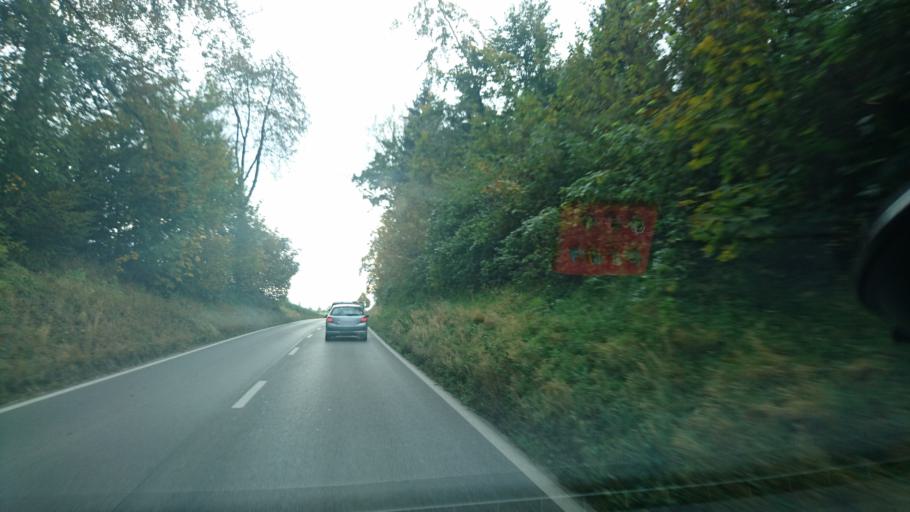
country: CH
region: Bern
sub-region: Bern-Mittelland District
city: Kirchlindach
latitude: 46.9848
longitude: 7.4134
